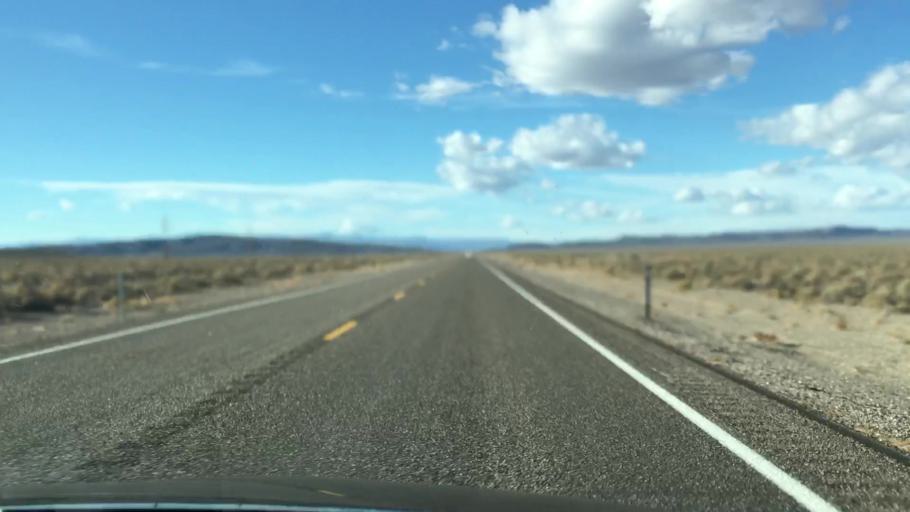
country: US
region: Nevada
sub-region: Nye County
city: Beatty
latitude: 37.1299
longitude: -116.8401
